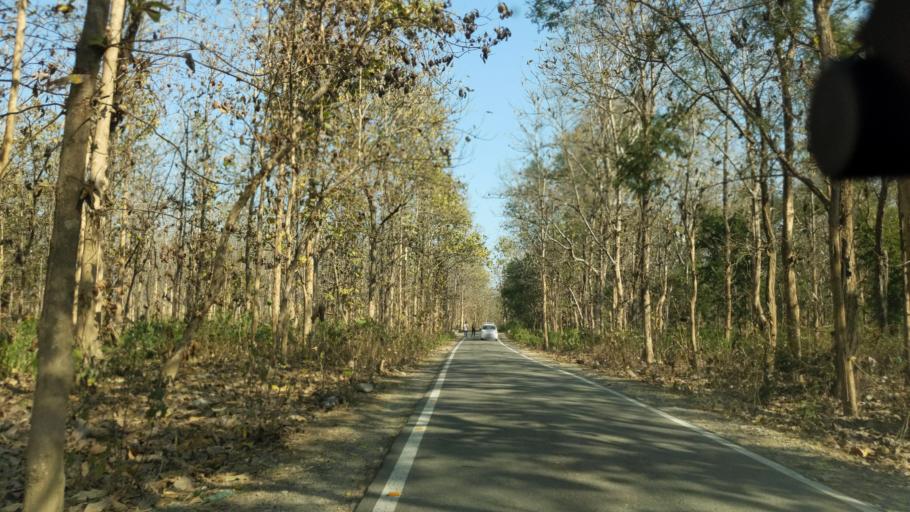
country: IN
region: Uttarakhand
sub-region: Naini Tal
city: Ramnagar
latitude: 29.4263
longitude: 79.1397
